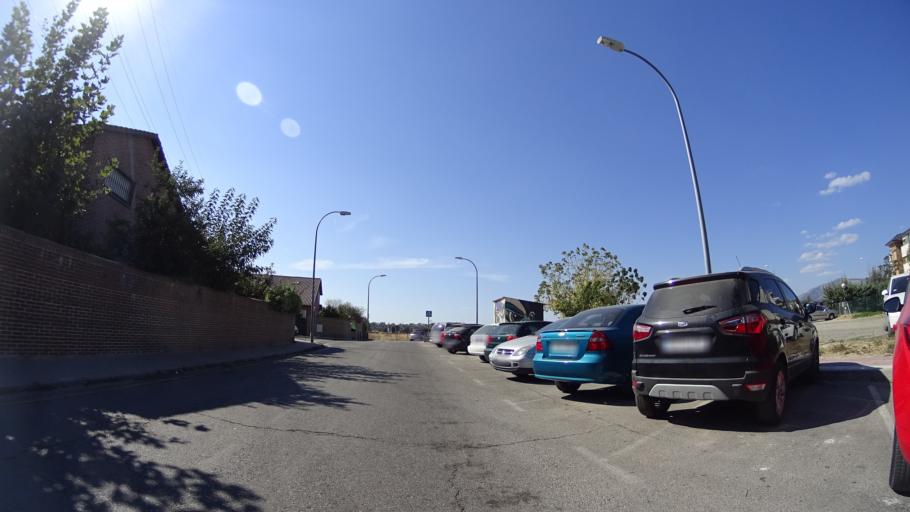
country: ES
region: Madrid
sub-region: Provincia de Madrid
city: Collado-Villalba
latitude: 40.6200
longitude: -4.0201
